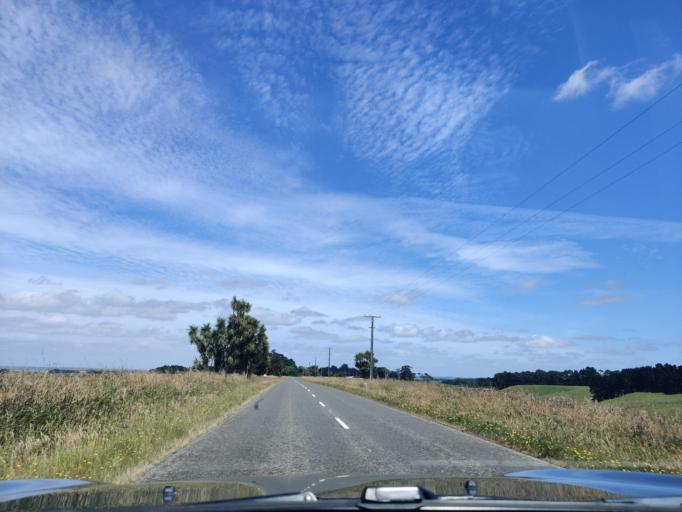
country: NZ
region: Manawatu-Wanganui
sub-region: Rangitikei District
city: Bulls
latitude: -40.1923
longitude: 175.4713
